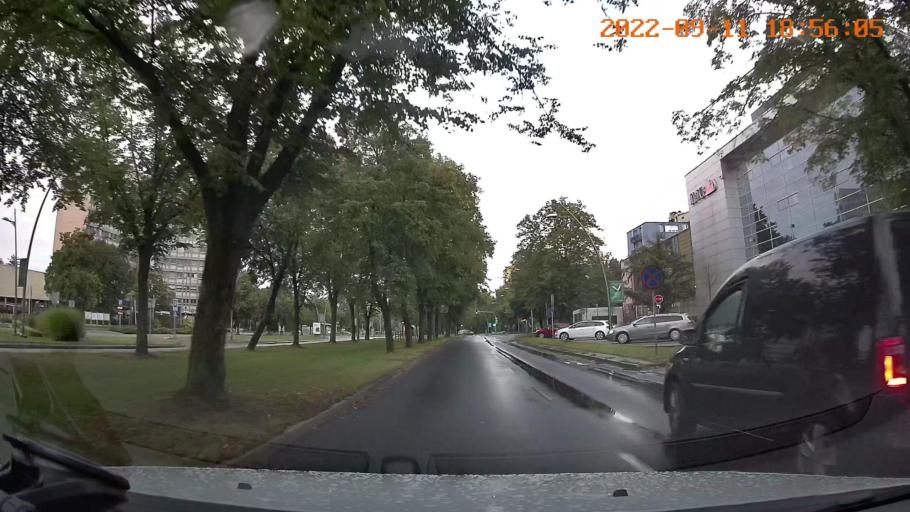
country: PL
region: Silesian Voivodeship
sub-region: Tychy
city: Cielmice
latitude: 50.1145
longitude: 18.9953
